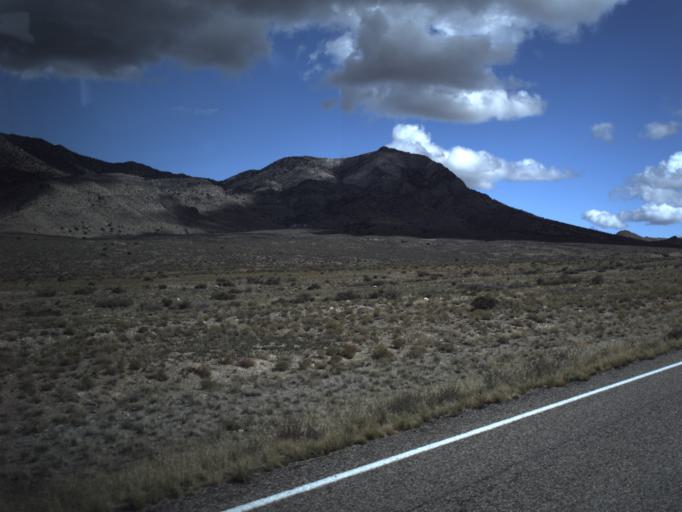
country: US
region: Utah
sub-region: Beaver County
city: Milford
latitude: 38.4429
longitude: -113.3230
